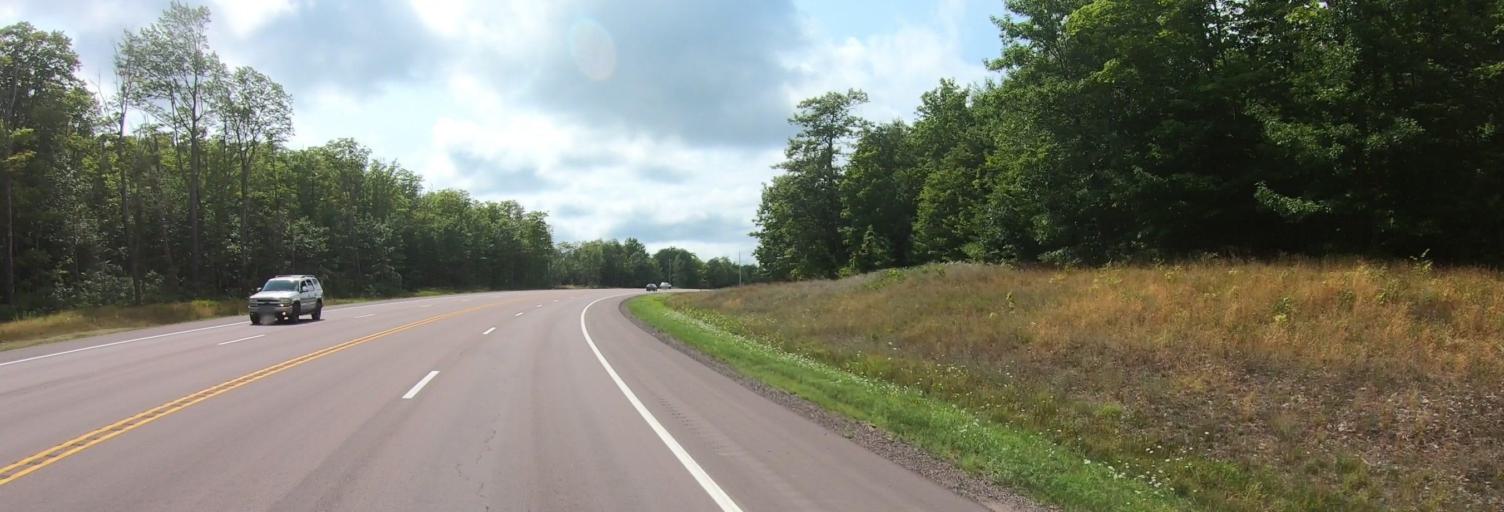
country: US
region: Michigan
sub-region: Houghton County
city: Hancock
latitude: 47.0595
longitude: -88.6447
